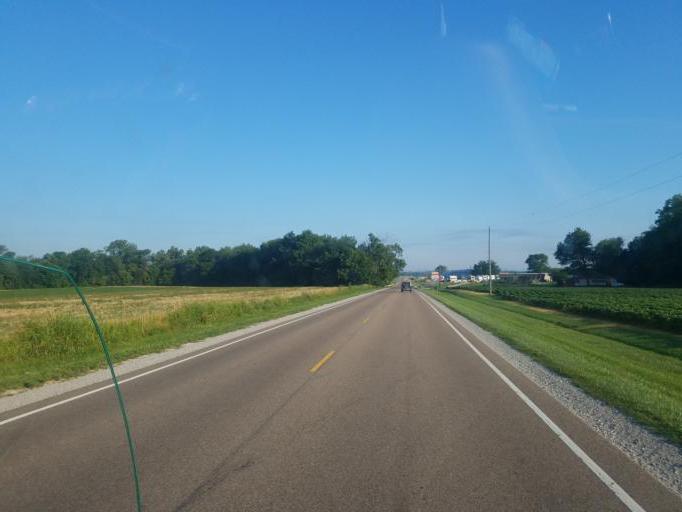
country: US
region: Illinois
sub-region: Bond County
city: Greenville
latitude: 38.8642
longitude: -89.3770
